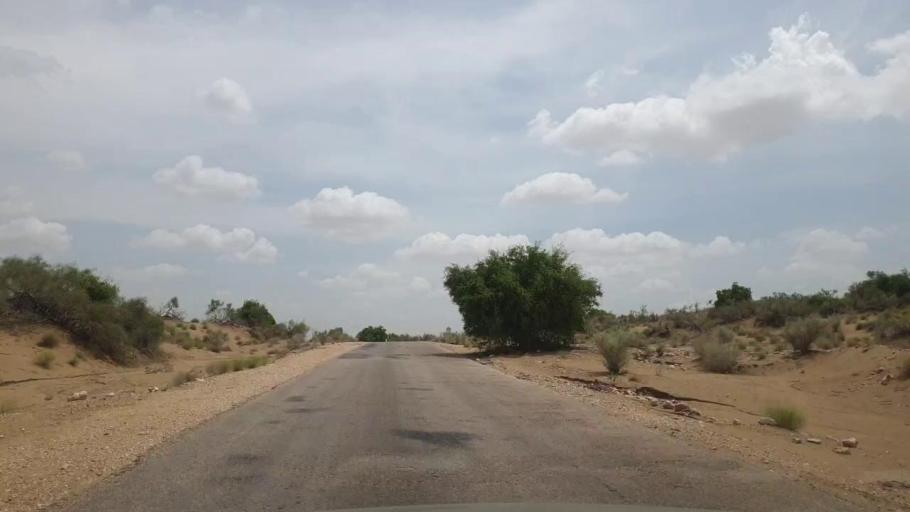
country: PK
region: Sindh
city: Kot Diji
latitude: 27.1598
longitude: 69.2232
